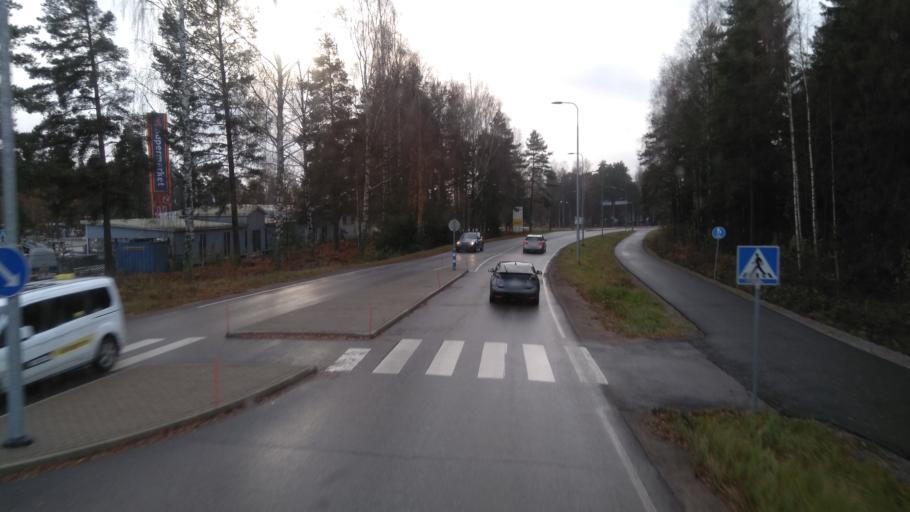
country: FI
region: Uusimaa
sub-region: Porvoo
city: Porvoo
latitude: 60.4006
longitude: 25.6851
